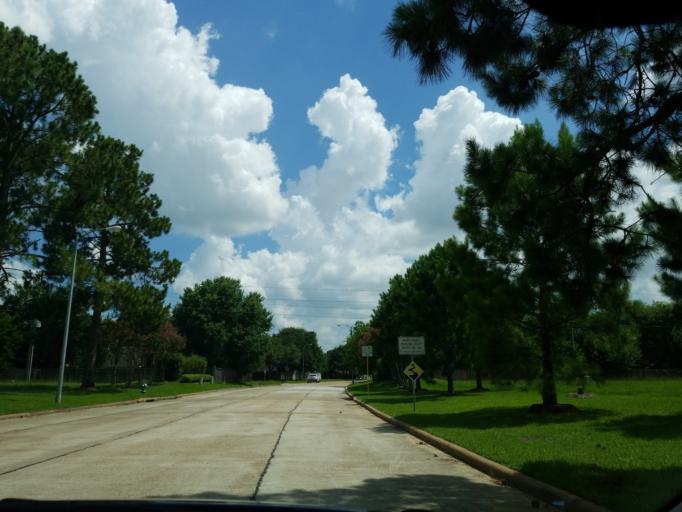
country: US
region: Texas
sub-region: Harris County
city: Cypress
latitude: 29.8785
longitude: -95.7319
